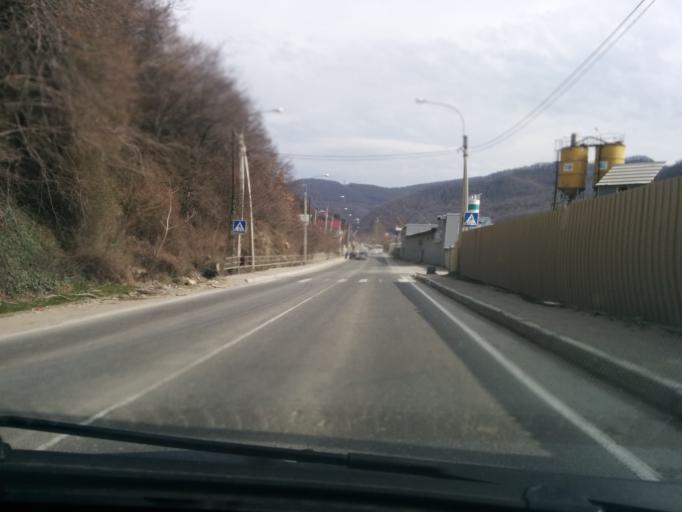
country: RU
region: Krasnodarskiy
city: Tuapse
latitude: 44.1174
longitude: 39.1106
